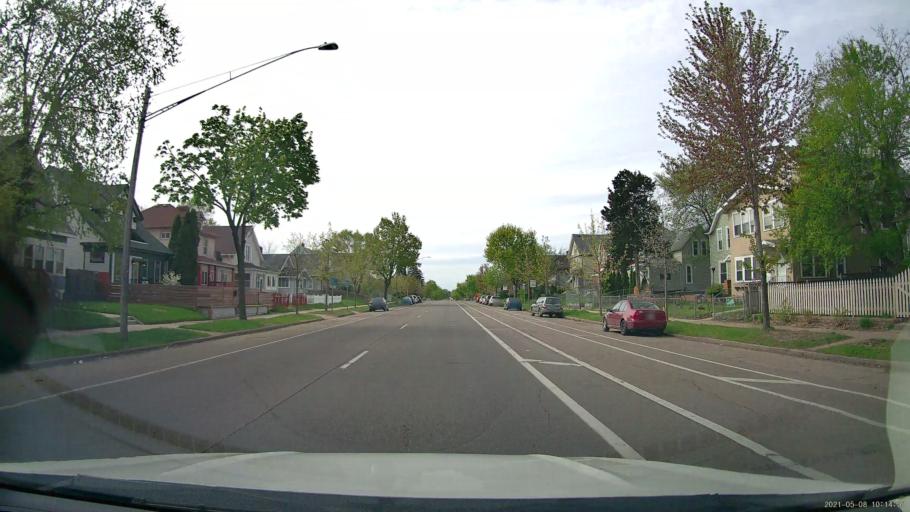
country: US
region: Minnesota
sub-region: Hennepin County
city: Minneapolis
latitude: 44.9336
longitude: -93.2675
